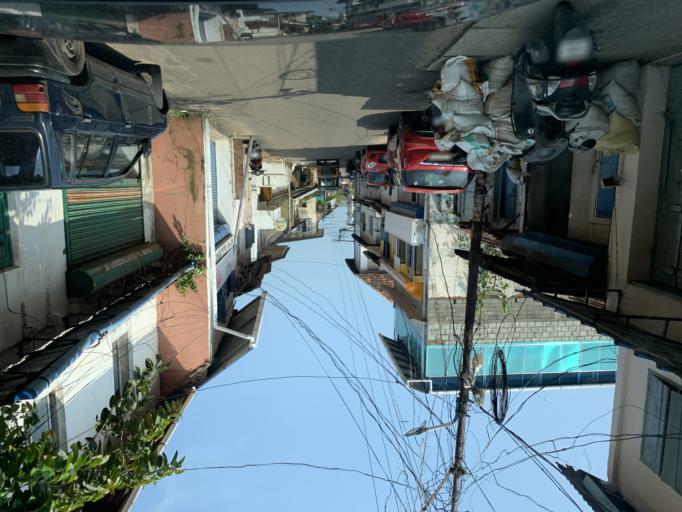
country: IN
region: Kerala
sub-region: Ernakulam
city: Cochin
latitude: 9.9535
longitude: 76.2605
